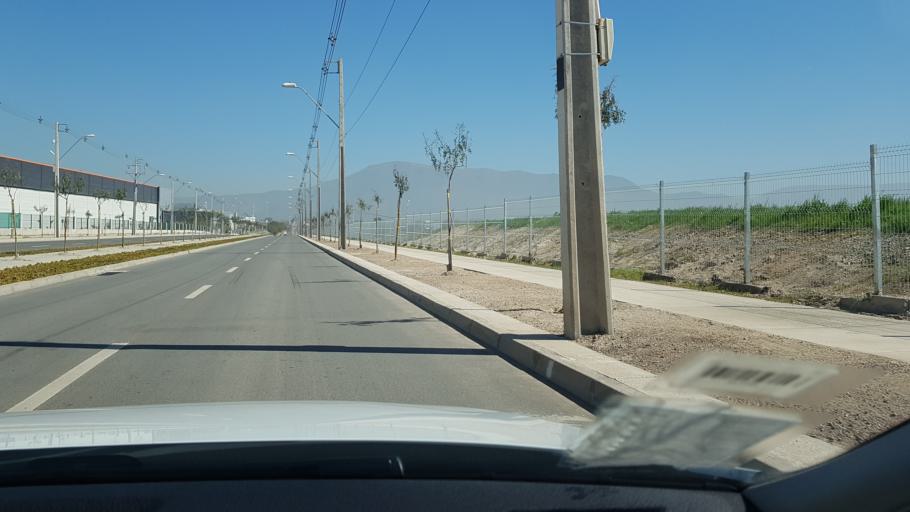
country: CL
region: Santiago Metropolitan
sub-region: Provincia de Santiago
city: Lo Prado
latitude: -33.4259
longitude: -70.7905
